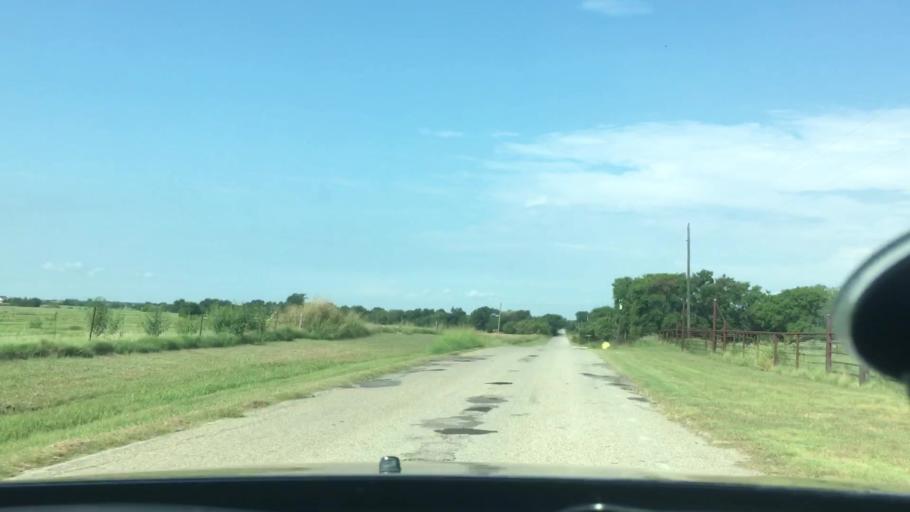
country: US
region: Oklahoma
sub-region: Bryan County
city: Calera
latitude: 33.9110
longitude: -96.4640
